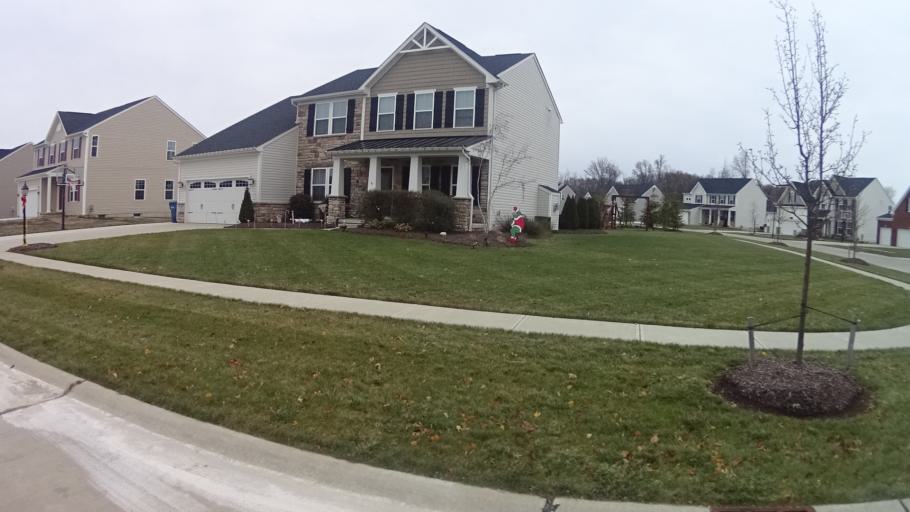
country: US
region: Ohio
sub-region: Lorain County
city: North Ridgeville
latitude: 41.3671
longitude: -81.9724
